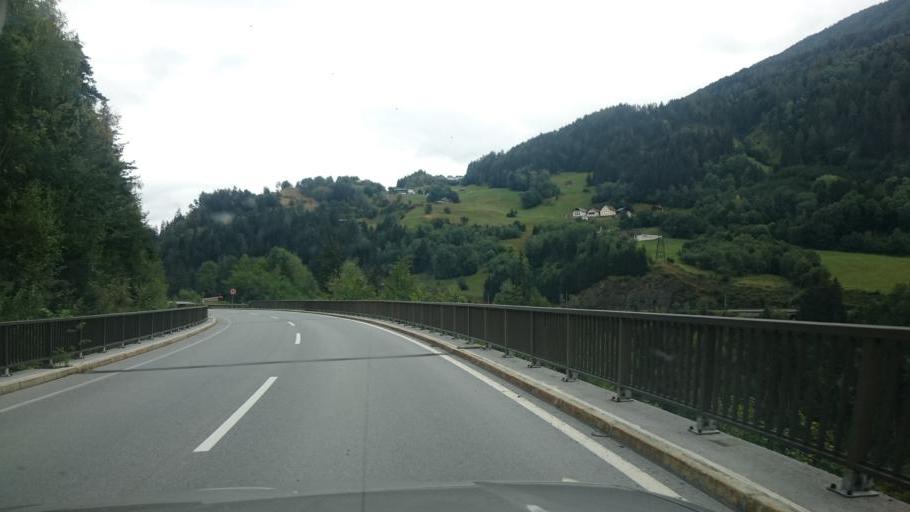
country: AT
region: Tyrol
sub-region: Politischer Bezirk Landeck
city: Tobadill
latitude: 47.1190
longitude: 10.4902
